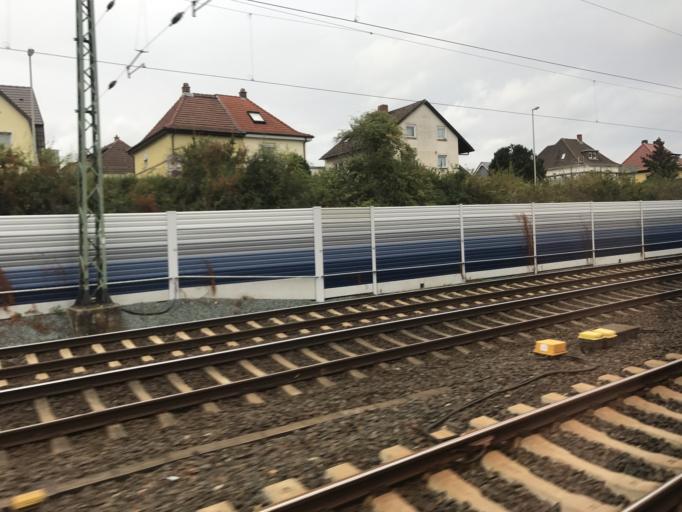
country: DE
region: Hesse
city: Kelsterbach
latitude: 50.0651
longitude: 8.5356
